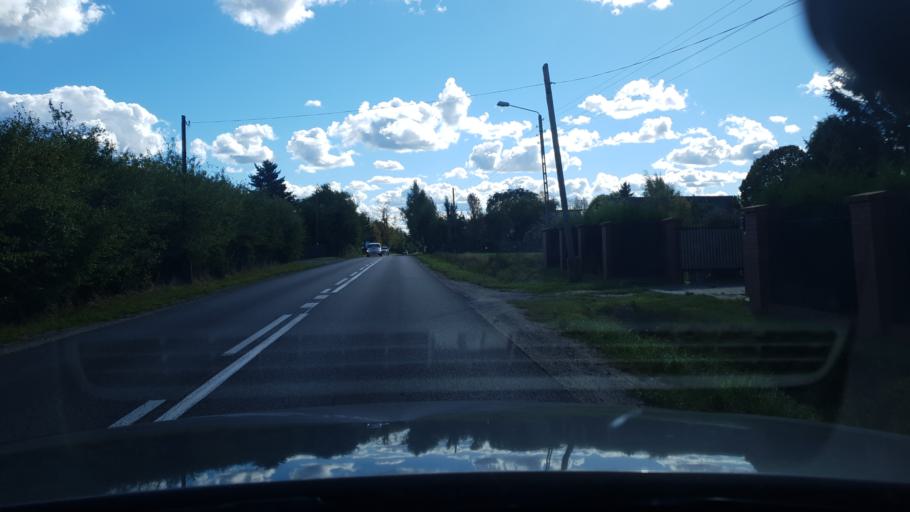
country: PL
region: Pomeranian Voivodeship
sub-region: Powiat pucki
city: Zelistrzewo
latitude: 54.6943
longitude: 18.4135
